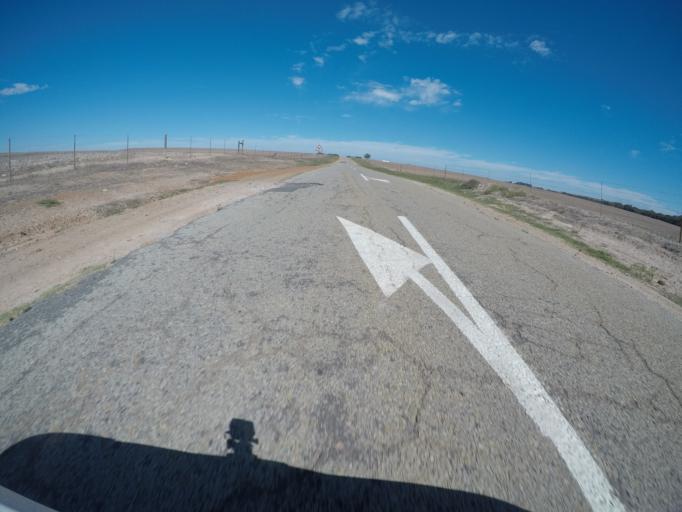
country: ZA
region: Western Cape
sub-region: City of Cape Town
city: Atlantis
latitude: -33.6037
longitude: 18.6402
